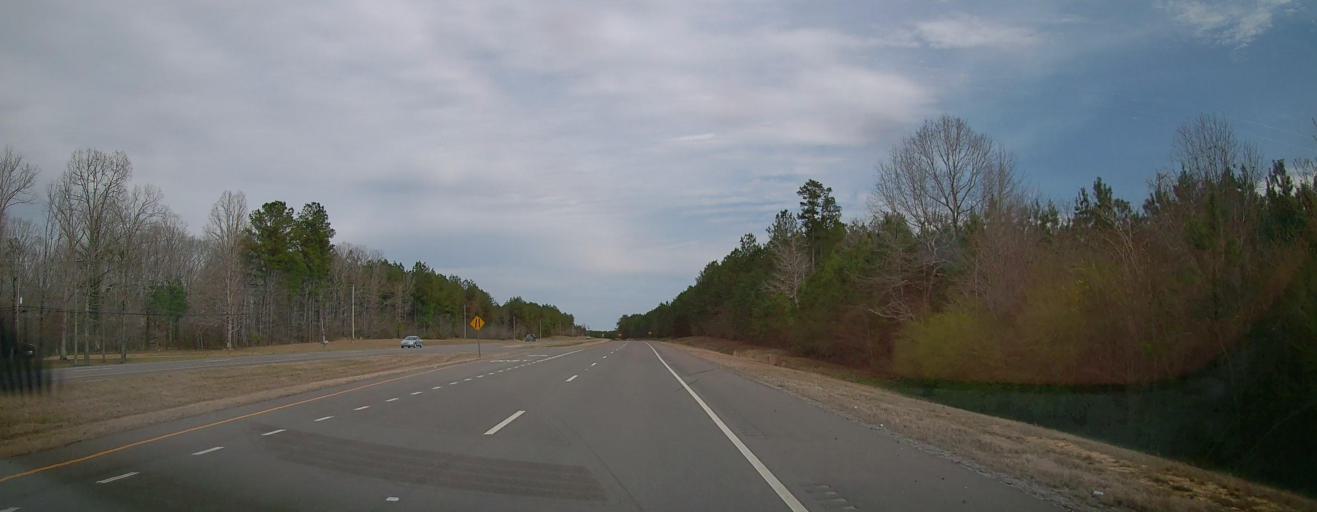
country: US
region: Alabama
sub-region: Walker County
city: Carbon Hill
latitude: 33.8677
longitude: -87.4282
